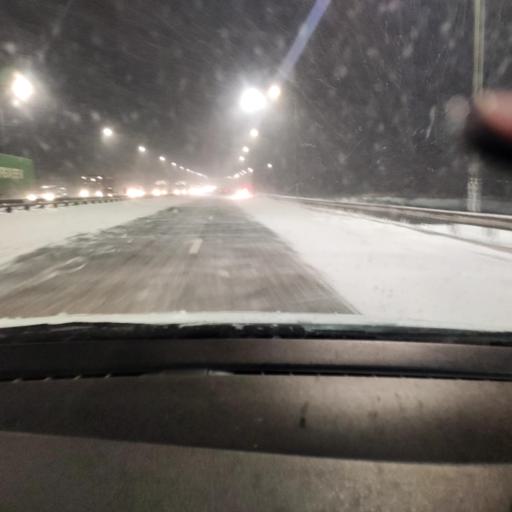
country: RU
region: Tatarstan
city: Pestretsy
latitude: 55.6741
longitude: 49.7044
